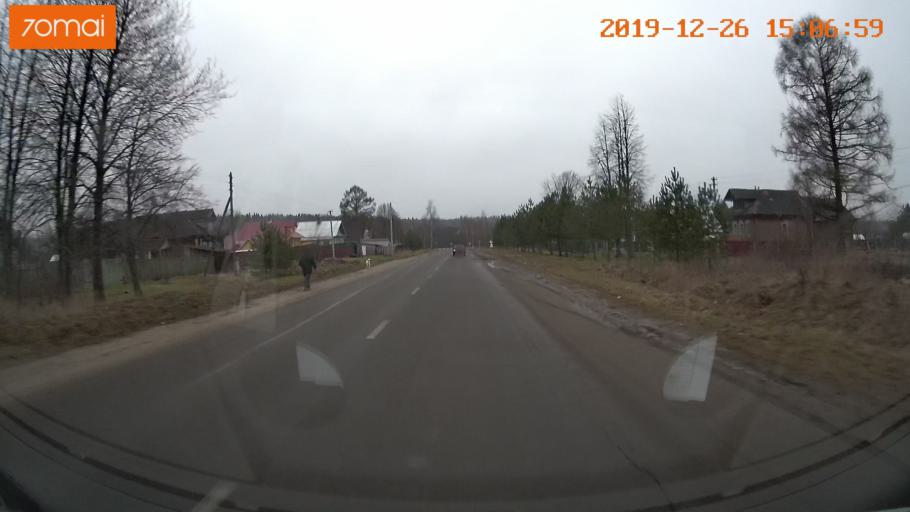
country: RU
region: Jaroslavl
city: Rybinsk
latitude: 58.1734
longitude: 38.8423
